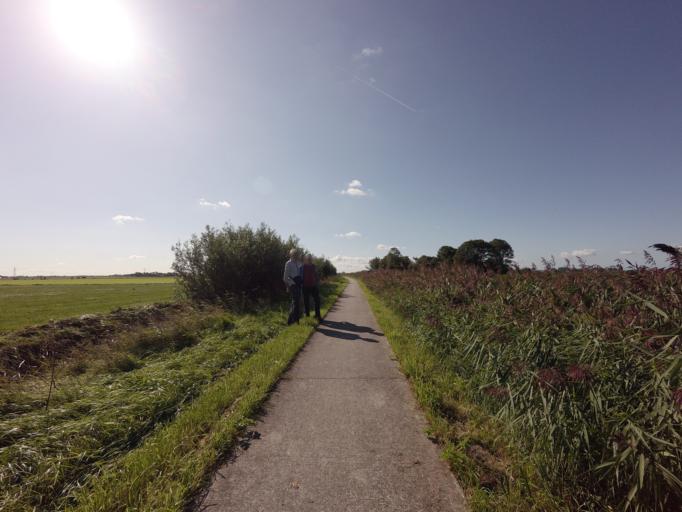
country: NL
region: Friesland
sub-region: Gemeente Boarnsterhim
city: Reduzum
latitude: 53.1298
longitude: 5.7559
